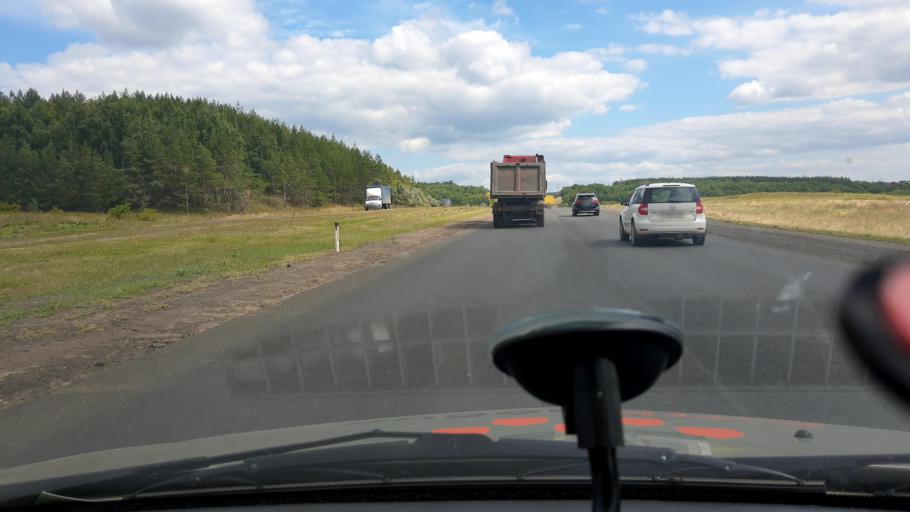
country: RU
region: Bashkortostan
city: Avdon
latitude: 54.6416
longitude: 55.5716
